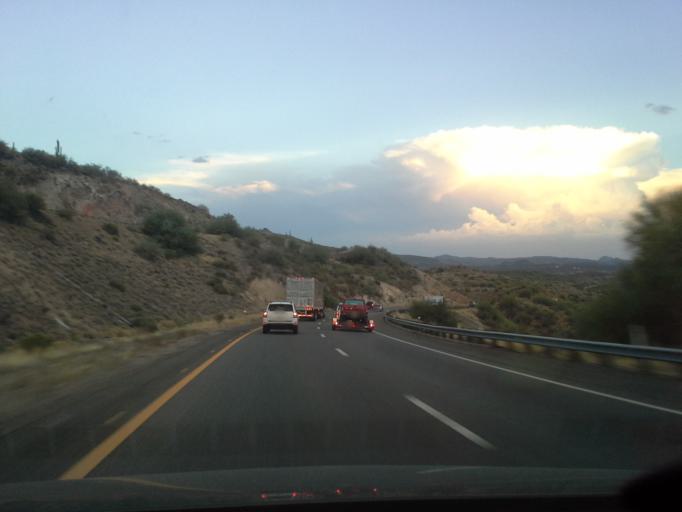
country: US
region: Arizona
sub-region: Yavapai County
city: Black Canyon City
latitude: 34.1128
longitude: -112.1447
